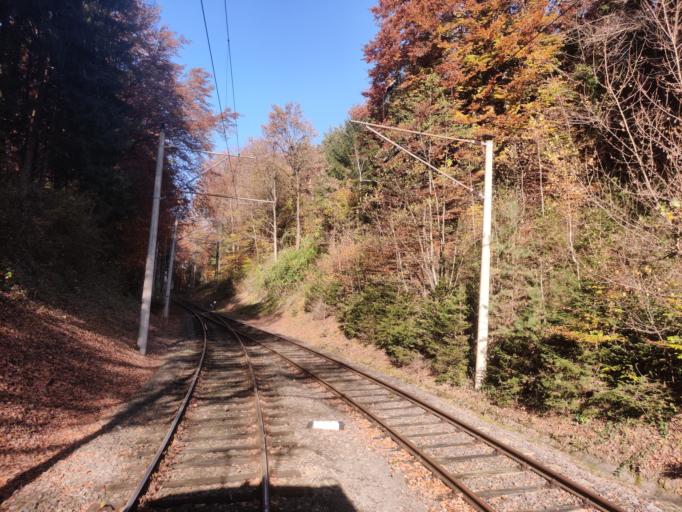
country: AT
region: Styria
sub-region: Politischer Bezirk Suedoststeiermark
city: Gnas
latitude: 46.8862
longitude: 15.8315
